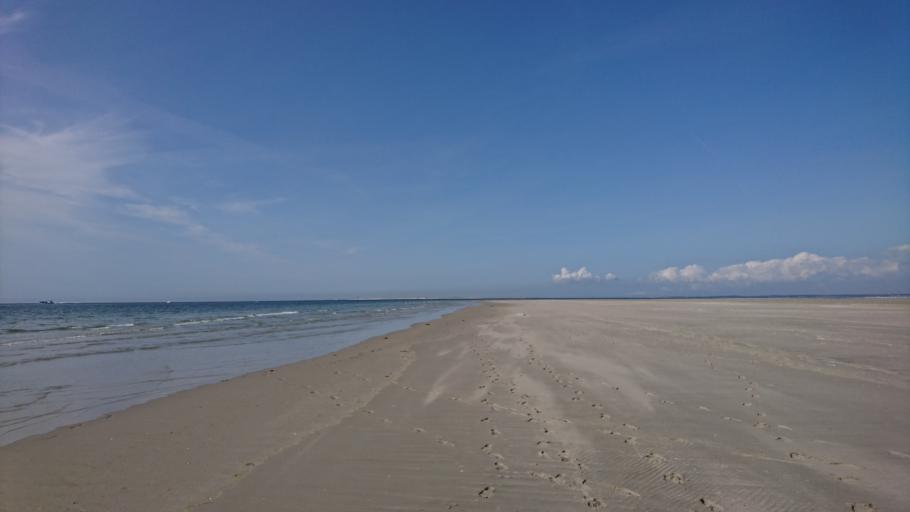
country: DK
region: South Denmark
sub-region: Fano Kommune
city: Nordby
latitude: 55.4487
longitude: 8.3284
